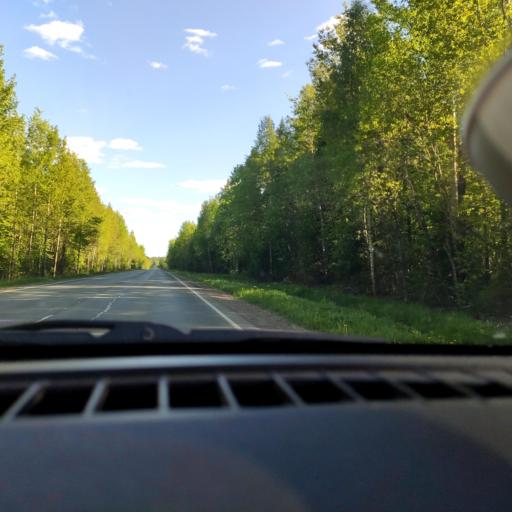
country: RU
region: Perm
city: Polazna
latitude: 58.2840
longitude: 56.1643
